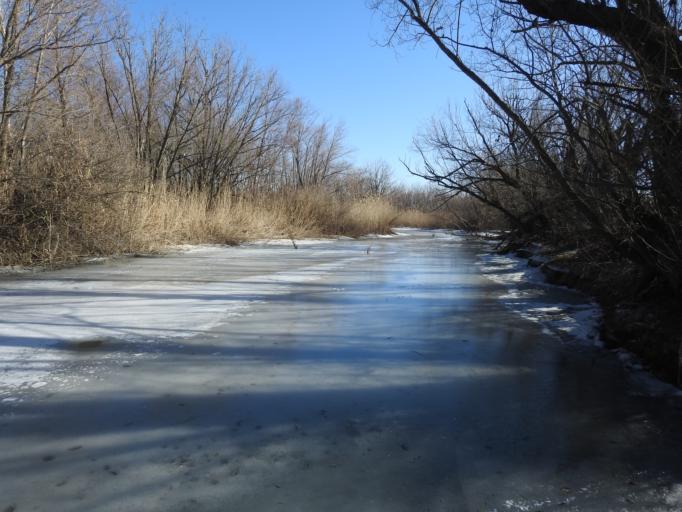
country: RU
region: Saratov
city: Yershov
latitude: 51.3377
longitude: 48.2285
